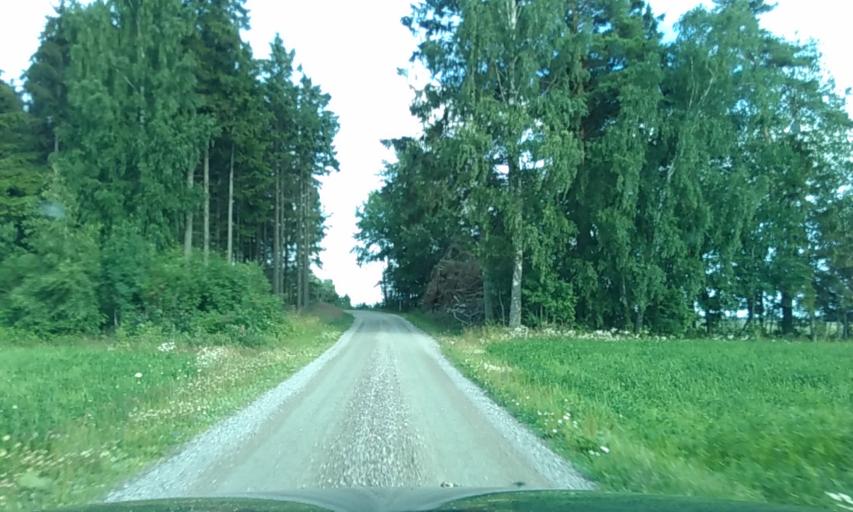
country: SE
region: Vaestra Goetaland
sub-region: Grastorps Kommun
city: Graestorp
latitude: 58.3775
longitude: 12.8003
